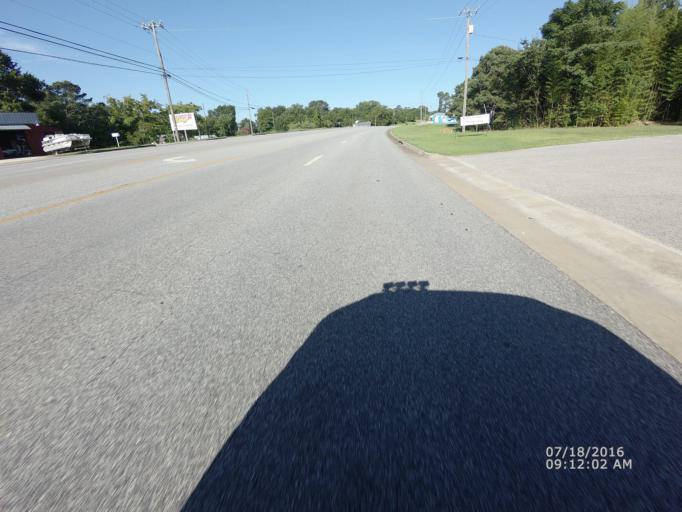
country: US
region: Alabama
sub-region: Chambers County
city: Huguley
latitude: 32.8472
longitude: -85.2178
